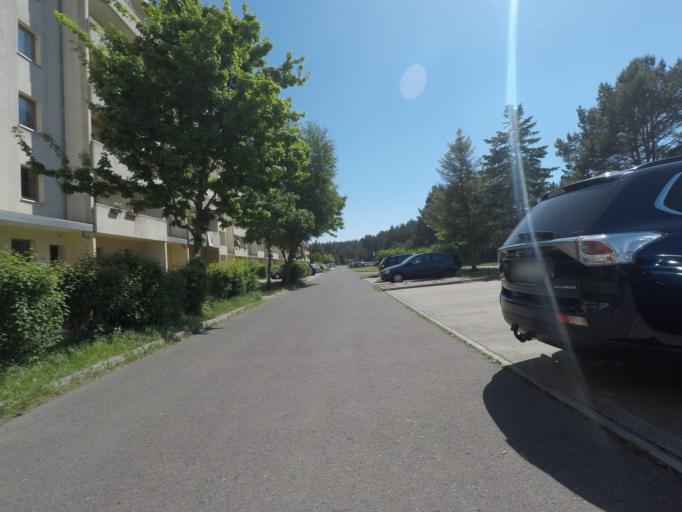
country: DE
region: Brandenburg
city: Eberswalde
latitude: 52.8313
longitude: 13.7521
